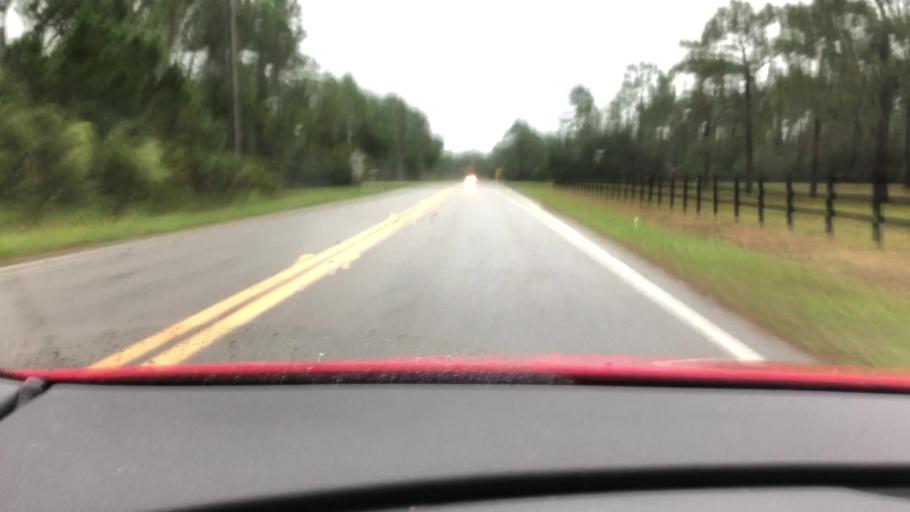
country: US
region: Florida
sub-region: Volusia County
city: Samsula-Spruce Creek
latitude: 29.0262
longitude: -81.1023
